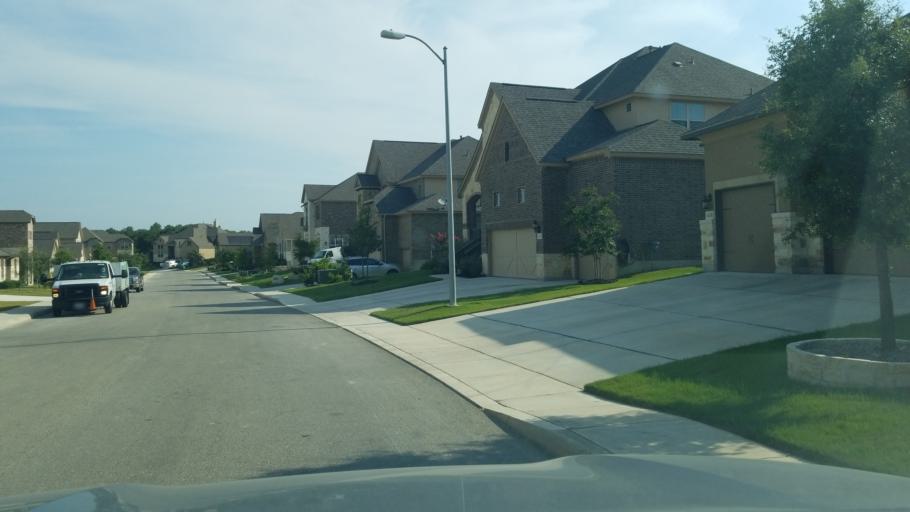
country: US
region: Texas
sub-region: Bexar County
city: Scenic Oaks
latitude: 29.6937
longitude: -98.6396
